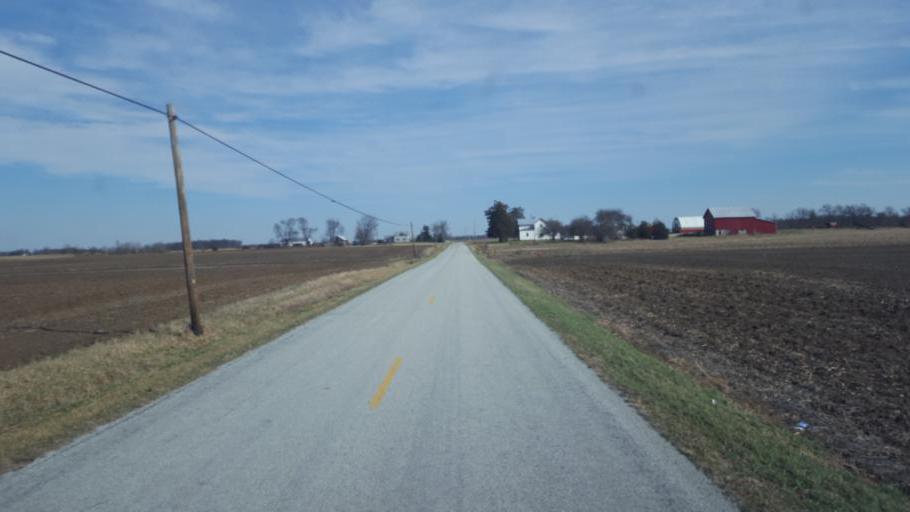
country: US
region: Ohio
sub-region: Hardin County
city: Kenton
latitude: 40.6575
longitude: -83.4911
